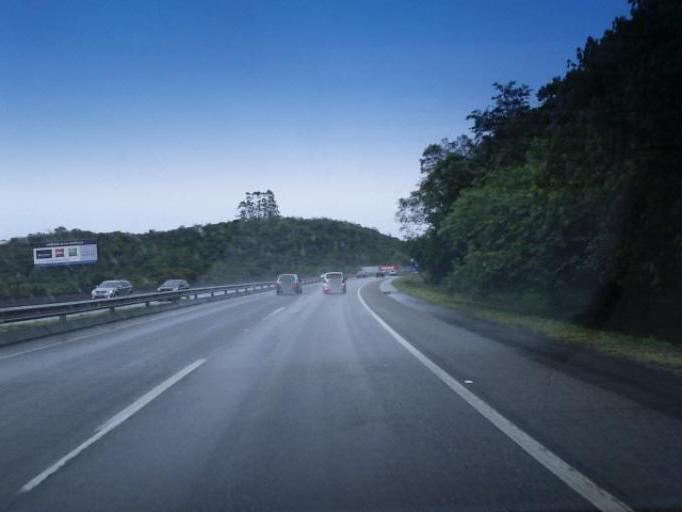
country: BR
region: Santa Catarina
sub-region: Joinville
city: Joinville
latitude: -26.4330
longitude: -48.8212
